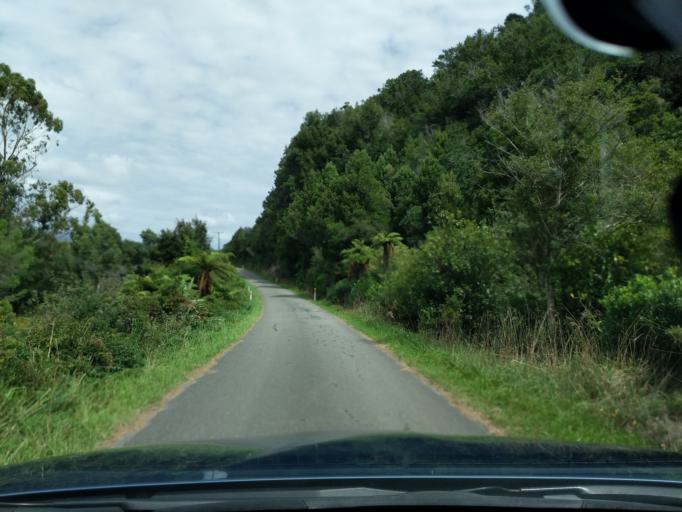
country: NZ
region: Tasman
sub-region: Tasman District
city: Takaka
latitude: -40.6398
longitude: 172.4857
